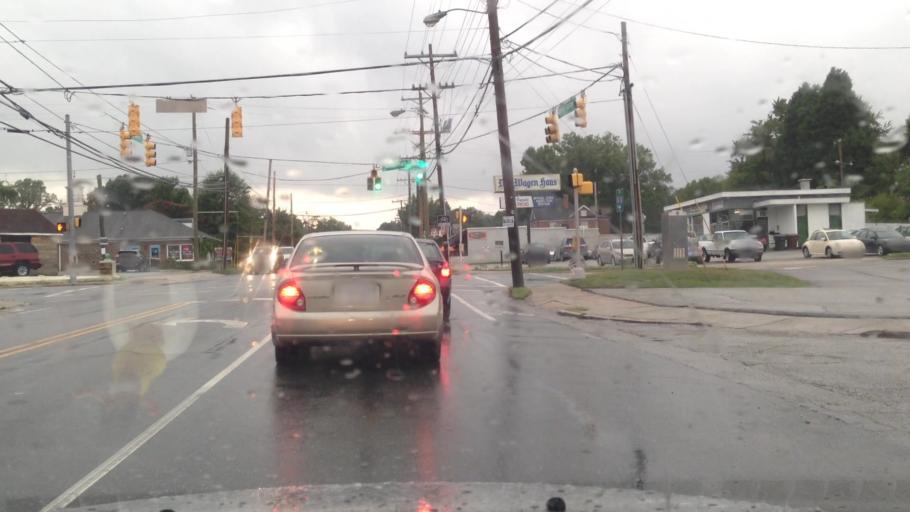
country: US
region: North Carolina
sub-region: Guilford County
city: Greensboro
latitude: 36.0638
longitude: -79.8233
